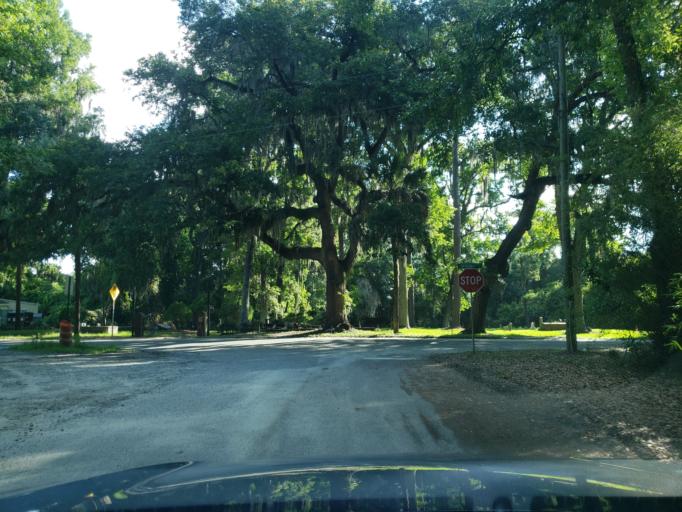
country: US
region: Georgia
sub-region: Chatham County
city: Isle of Hope
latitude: 31.9845
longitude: -81.0735
